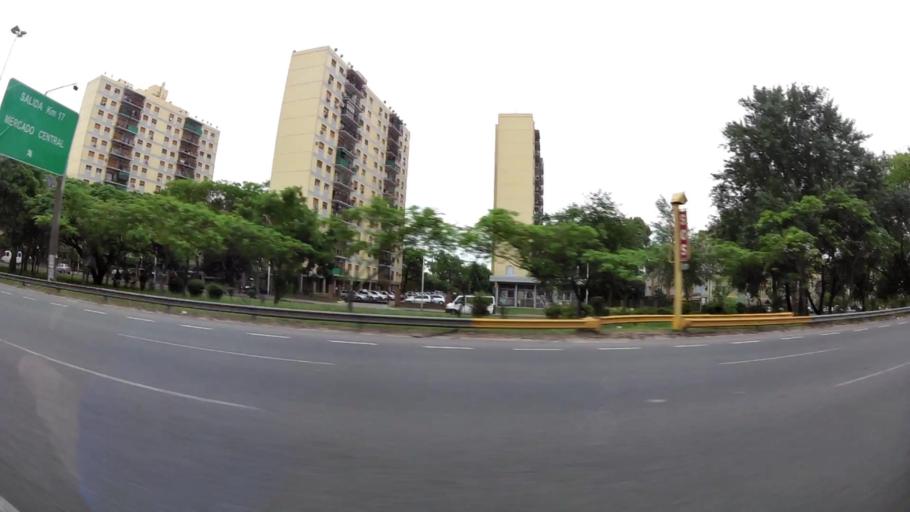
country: AR
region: Buenos Aires F.D.
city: Villa Lugano
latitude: -34.7052
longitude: -58.5006
